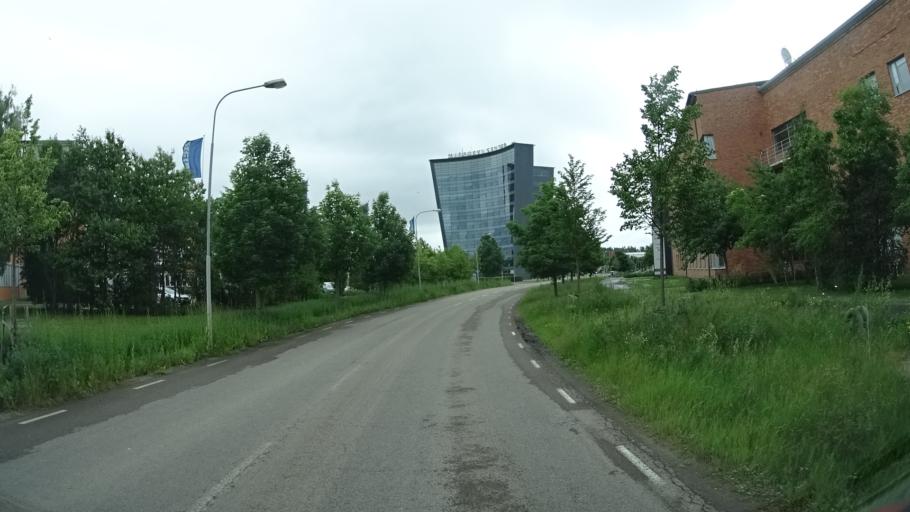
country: SE
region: OEstergoetland
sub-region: Linkopings Kommun
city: Malmslatt
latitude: 58.3927
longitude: 15.5572
